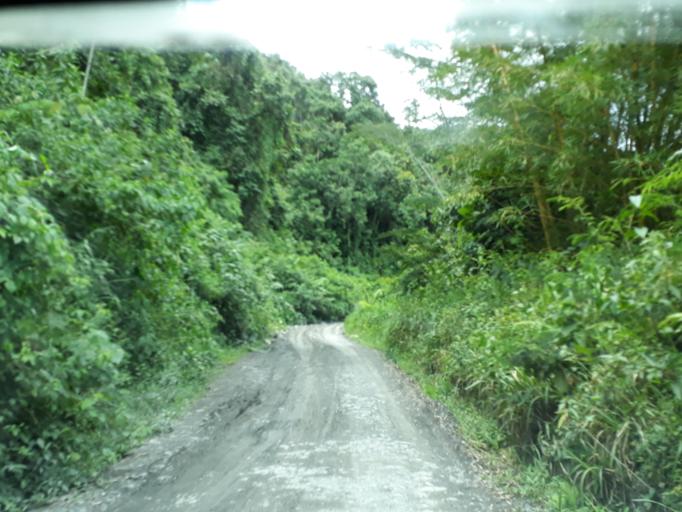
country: CO
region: Cundinamarca
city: Topaipi
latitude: 5.3445
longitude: -74.1875
